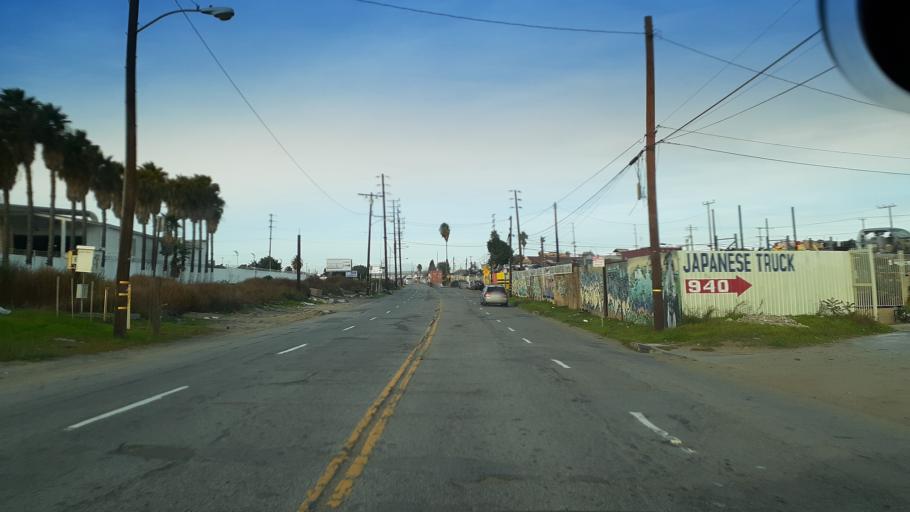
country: US
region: California
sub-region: Los Angeles County
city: Long Beach
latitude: 33.7826
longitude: -118.2444
